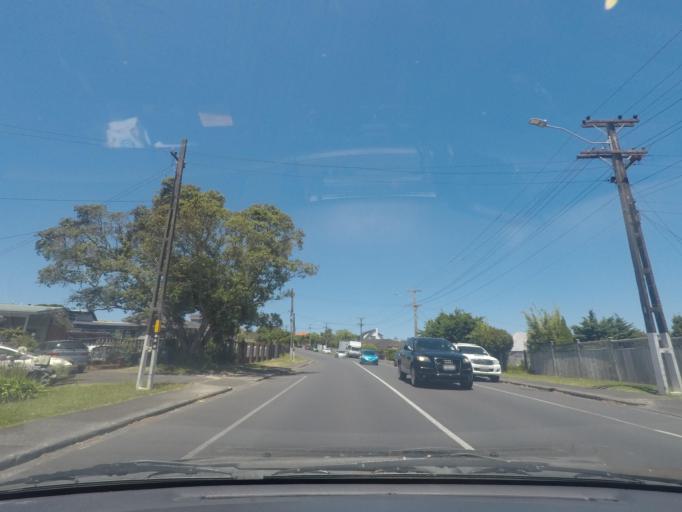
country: NZ
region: Auckland
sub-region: Auckland
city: Auckland
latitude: -36.9301
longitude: 174.7307
